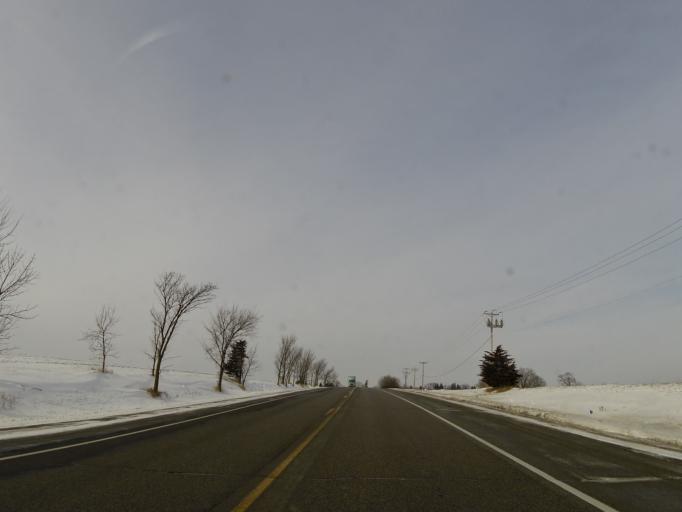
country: US
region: Minnesota
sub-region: Hennepin County
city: Saint Bonifacius
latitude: 44.8958
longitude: -93.7148
